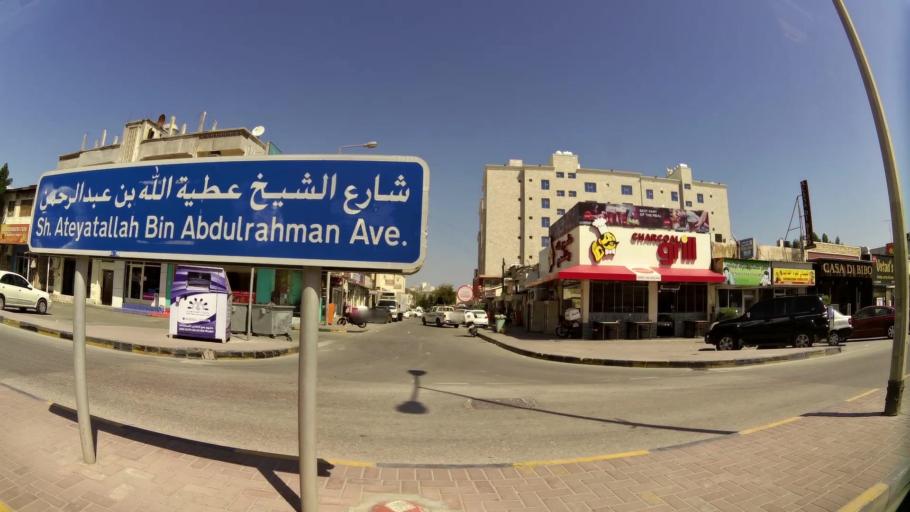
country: BH
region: Manama
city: Manama
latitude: 26.2053
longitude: 50.5960
